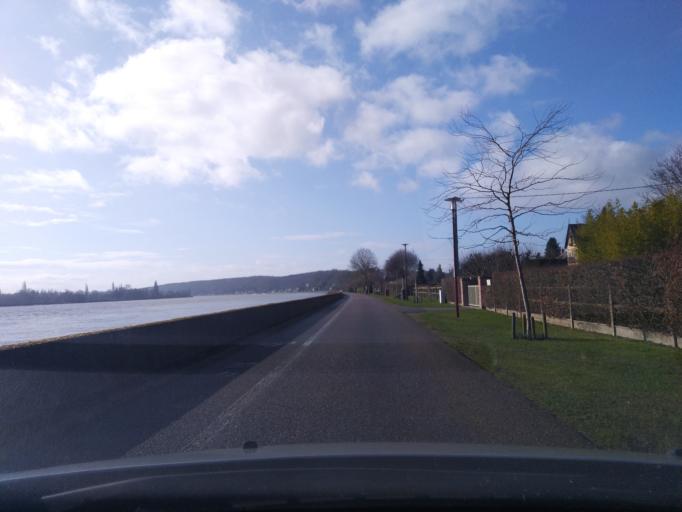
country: FR
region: Haute-Normandie
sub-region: Departement de la Seine-Maritime
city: Duclair
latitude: 49.4744
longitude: 0.8653
